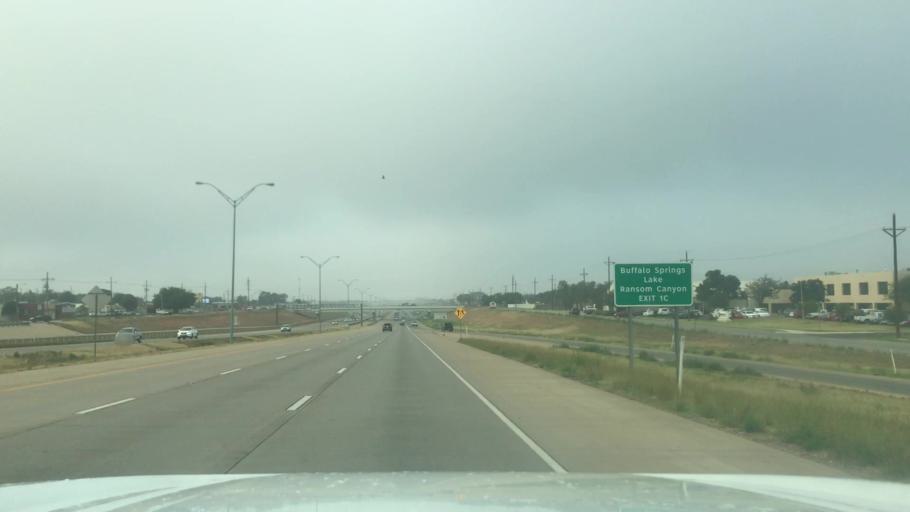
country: US
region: Texas
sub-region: Lubbock County
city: Lubbock
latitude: 33.5606
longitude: -101.8452
